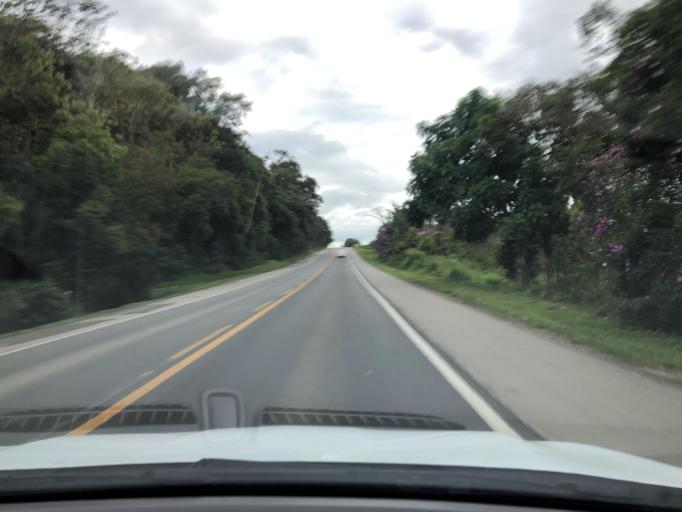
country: BR
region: Santa Catarina
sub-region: Joinville
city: Joinville
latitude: -26.4313
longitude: -48.7991
